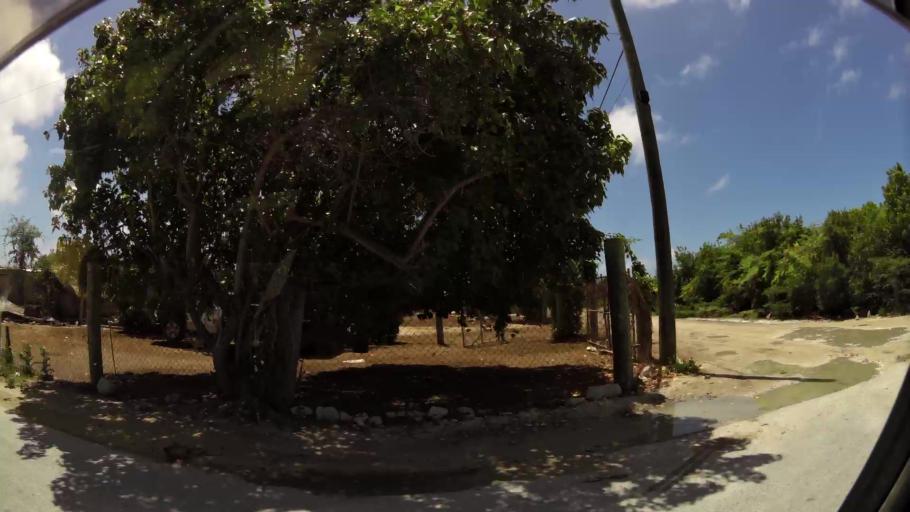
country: TC
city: Cockburn Town
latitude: 21.4587
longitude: -71.1443
